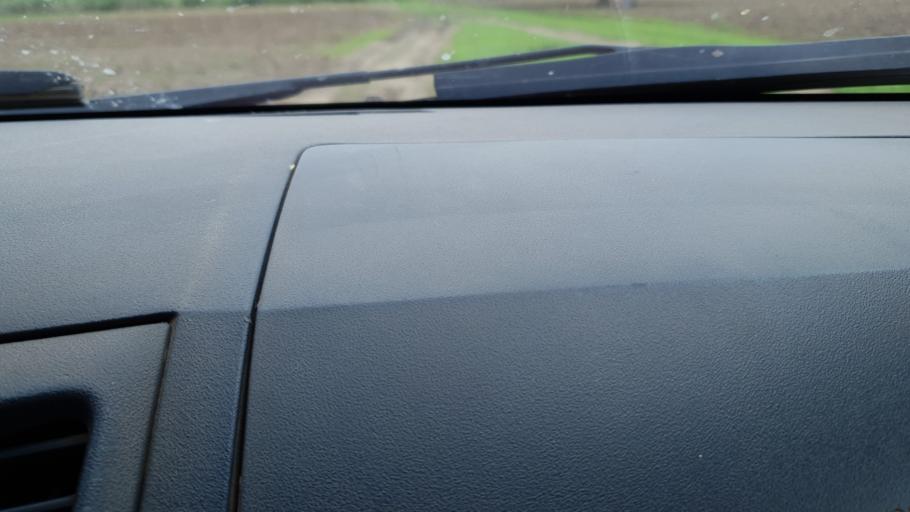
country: ML
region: Segou
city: Baroueli
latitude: 13.3461
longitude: -7.0937
